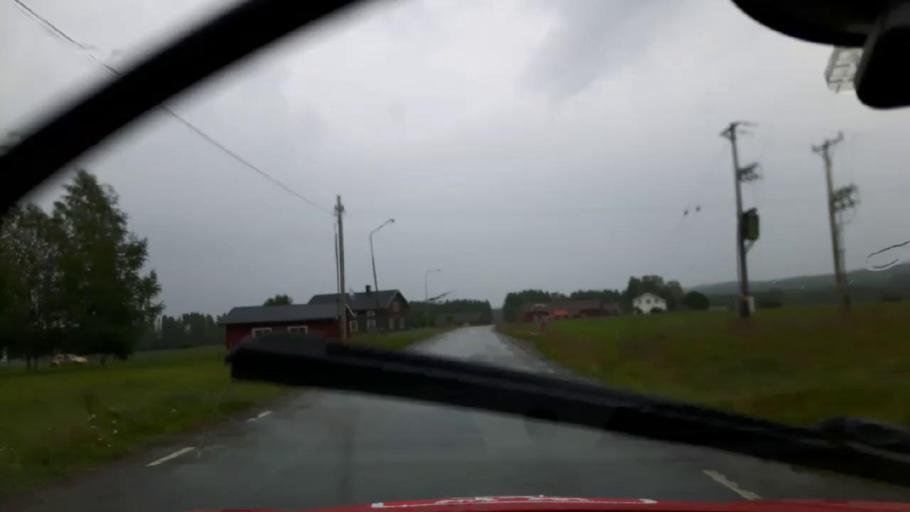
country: SE
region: Jaemtland
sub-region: OEstersunds Kommun
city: Brunflo
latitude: 62.9860
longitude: 14.8129
